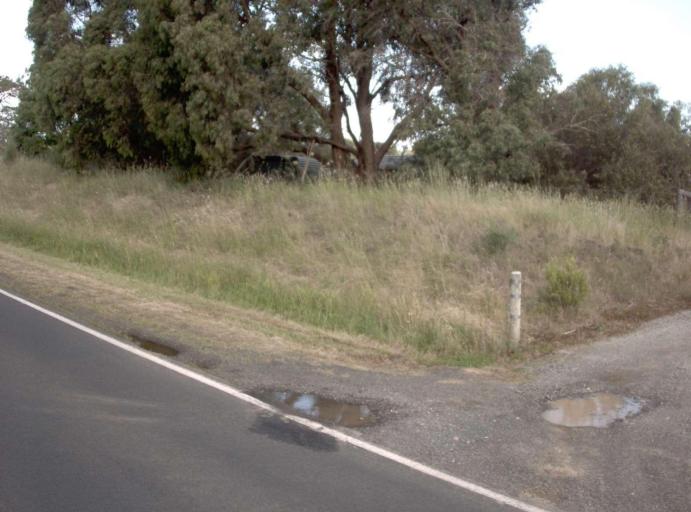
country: AU
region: Victoria
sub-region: Bass Coast
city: North Wonthaggi
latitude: -38.6059
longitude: 145.7642
